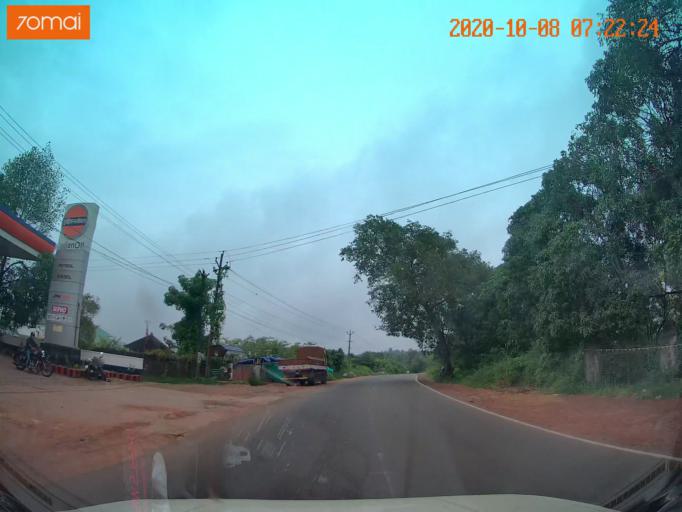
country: IN
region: Kerala
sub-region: Malappuram
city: Tirur
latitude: 10.8640
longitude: 76.0386
